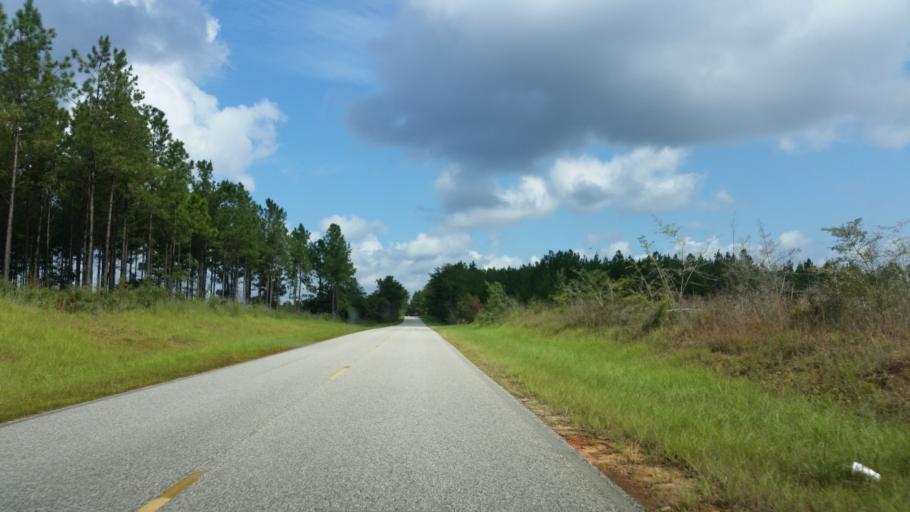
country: US
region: Florida
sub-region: Escambia County
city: Cantonment
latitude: 30.6759
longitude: -87.4704
